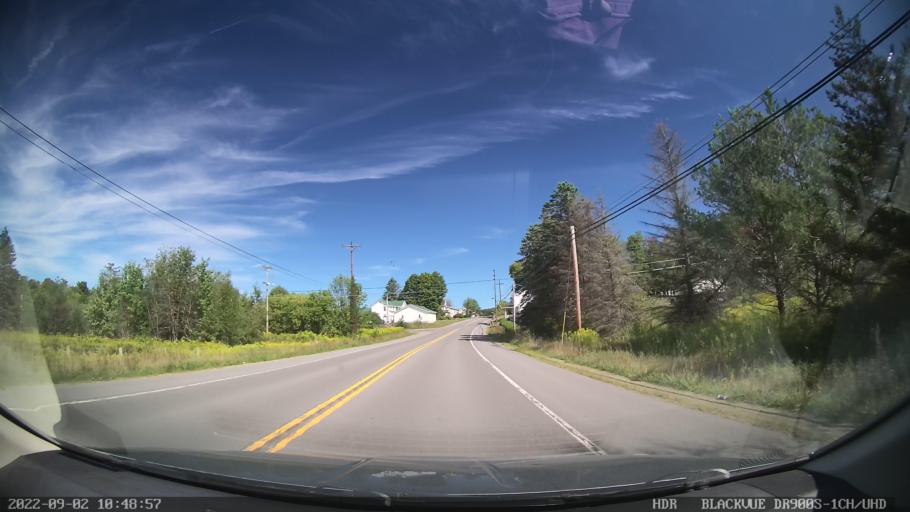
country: US
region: Pennsylvania
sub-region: Tioga County
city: Blossburg
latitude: 41.5939
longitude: -77.1100
